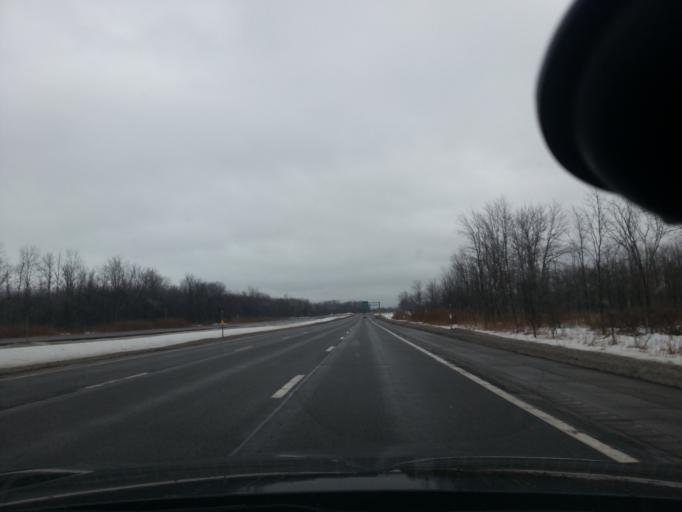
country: US
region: New York
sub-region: Onondaga County
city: Brewerton
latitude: 43.2634
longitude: -76.1314
